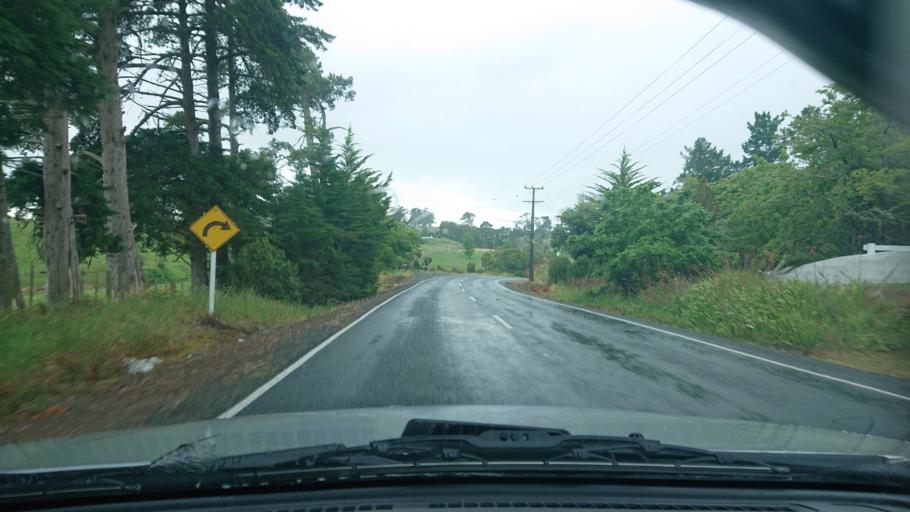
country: NZ
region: Auckland
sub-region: Auckland
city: Wellsford
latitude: -36.2853
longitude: 174.4595
